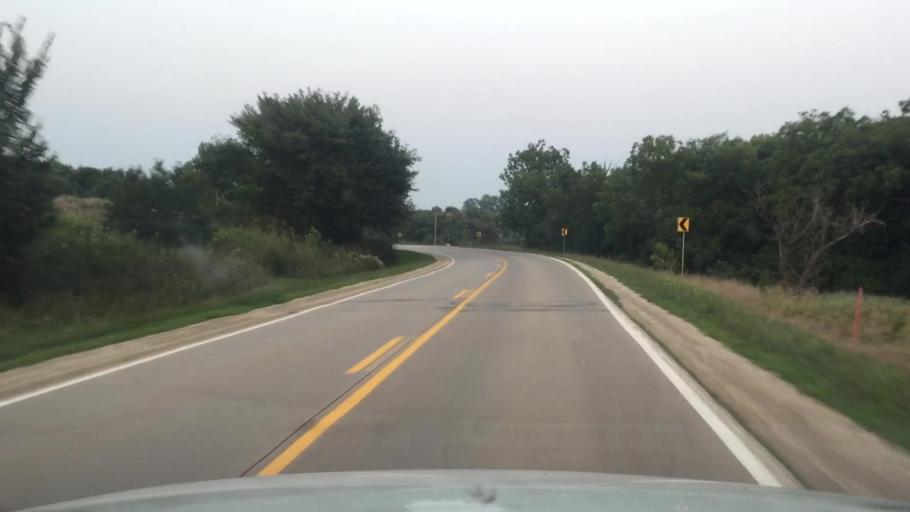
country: US
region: Iowa
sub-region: Clarke County
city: Osceola
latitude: 41.1802
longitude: -93.7136
